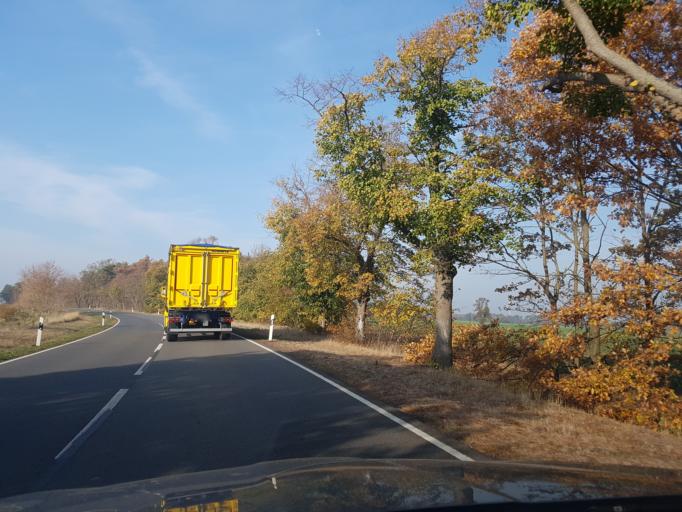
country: DE
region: Brandenburg
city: Bad Liebenwerda
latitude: 51.5277
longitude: 13.3277
